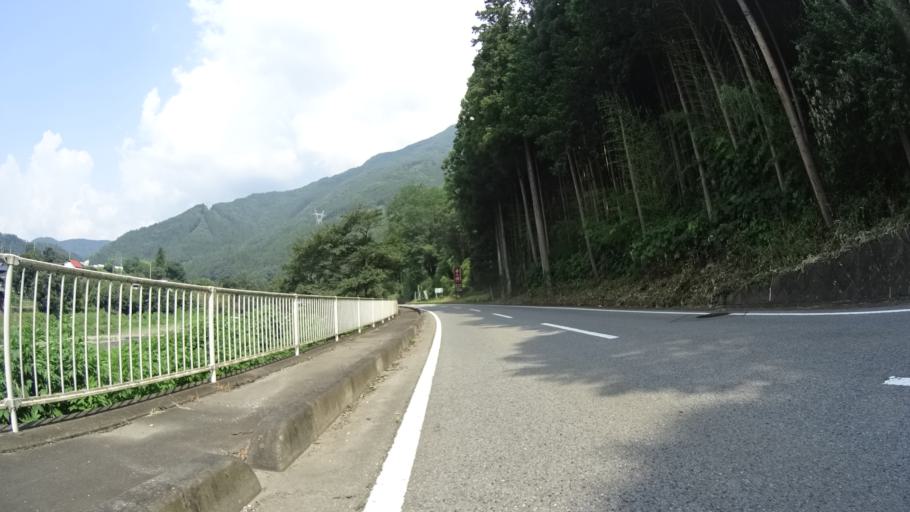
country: JP
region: Gunma
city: Tomioka
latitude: 36.0829
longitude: 138.7924
